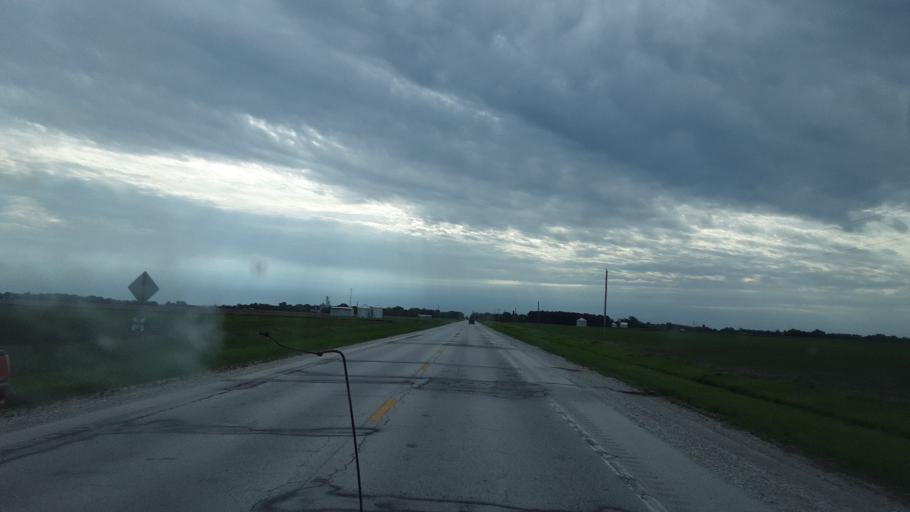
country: US
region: Illinois
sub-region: Hancock County
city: Hamilton
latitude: 40.3952
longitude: -91.2707
